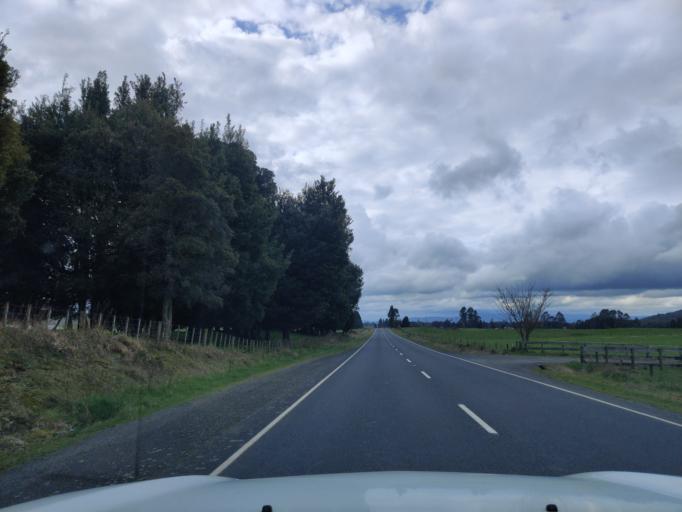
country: NZ
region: Waikato
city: Turangi
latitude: -39.0394
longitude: 175.3831
